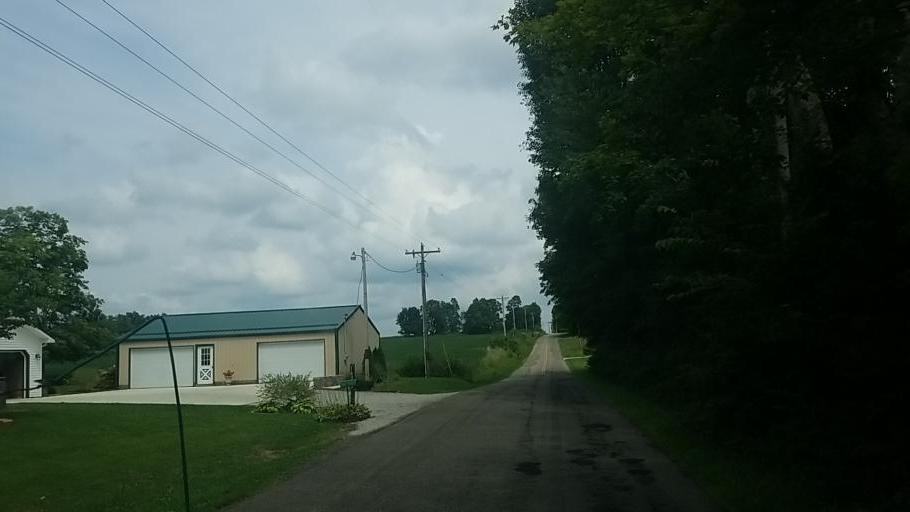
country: US
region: Ohio
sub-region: Knox County
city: Mount Vernon
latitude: 40.3212
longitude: -82.4650
